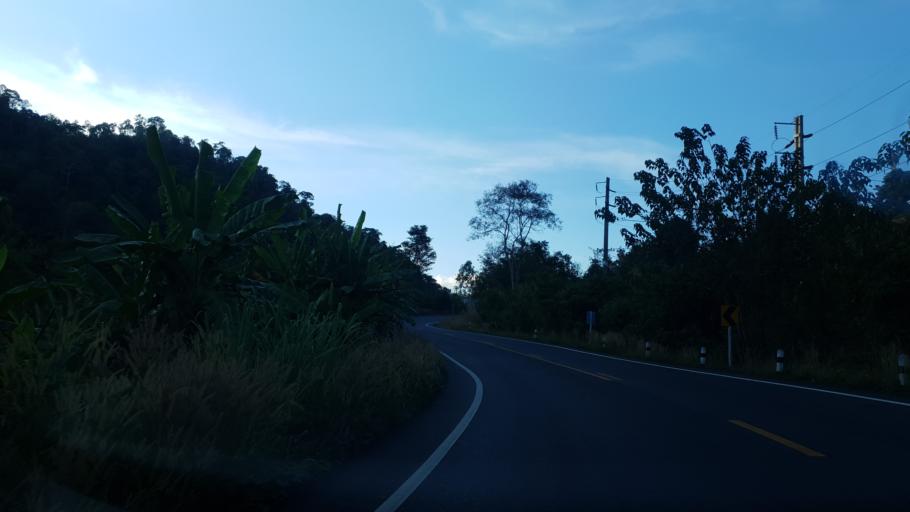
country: TH
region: Loei
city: Dan Sai
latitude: 17.2270
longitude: 101.0595
